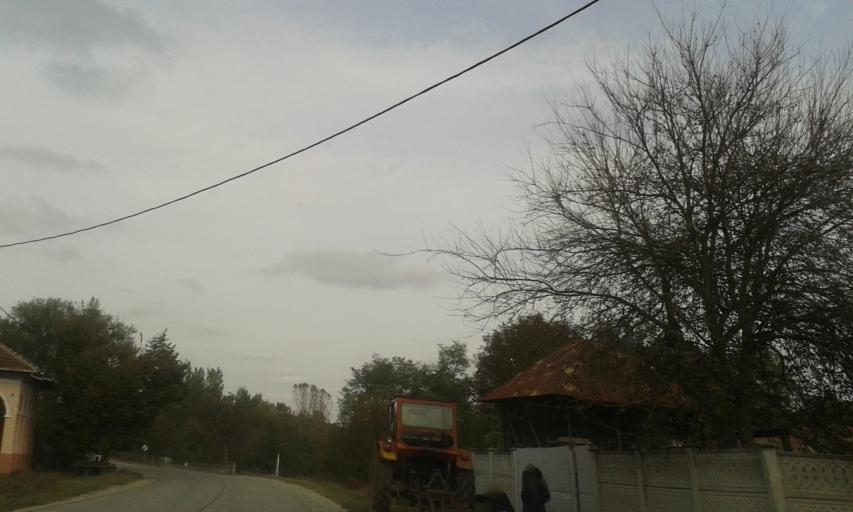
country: RO
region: Gorj
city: Logresti
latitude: 44.8819
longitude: 23.7122
